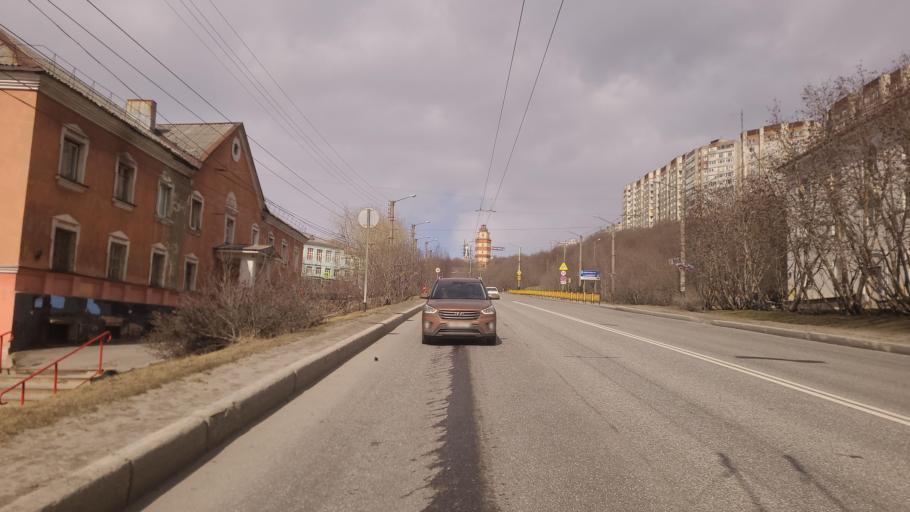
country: RU
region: Murmansk
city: Murmansk
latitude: 68.9821
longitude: 33.0933
